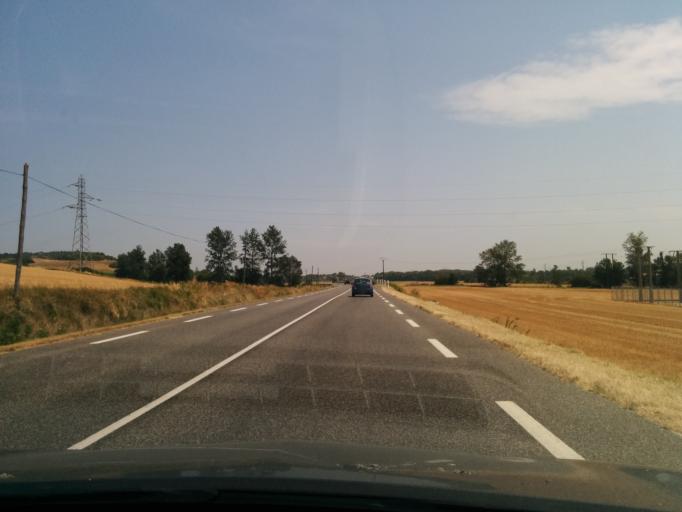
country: FR
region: Midi-Pyrenees
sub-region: Departement de la Haute-Garonne
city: Avignonet-Lauragais
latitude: 43.3634
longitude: 1.7937
